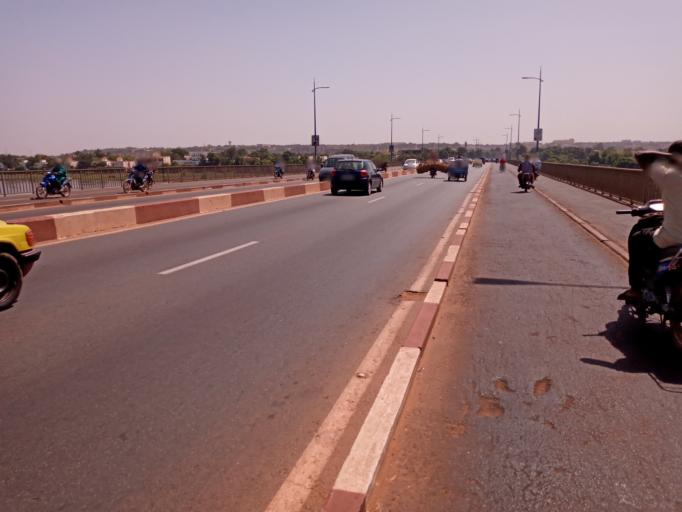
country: ML
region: Bamako
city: Bamako
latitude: 12.6224
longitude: -8.0040
